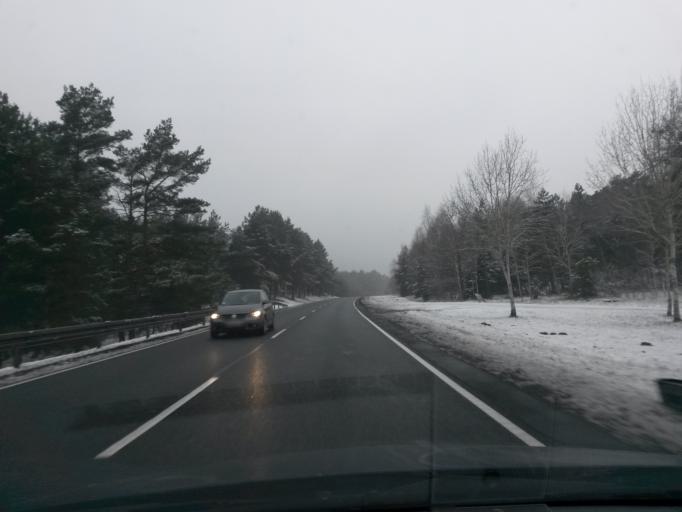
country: PL
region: Kujawsko-Pomorskie
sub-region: Powiat torunski
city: Zlawies Wielka
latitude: 53.0504
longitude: 18.3430
